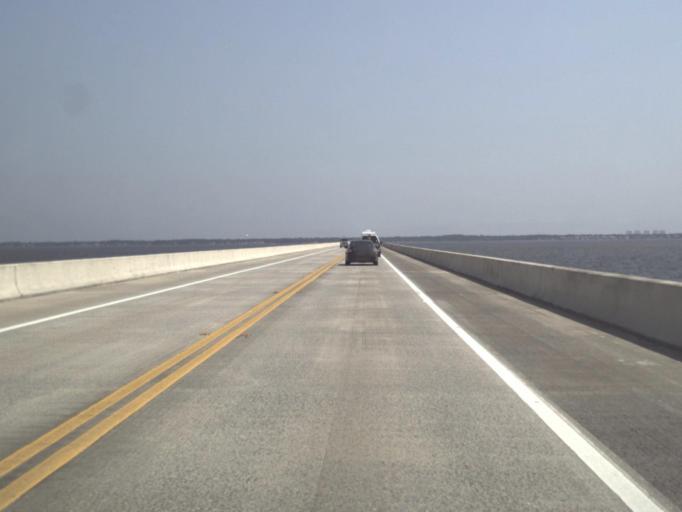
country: US
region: Florida
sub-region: Santa Rosa County
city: Oriole Beach
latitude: 30.4331
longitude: -87.0973
